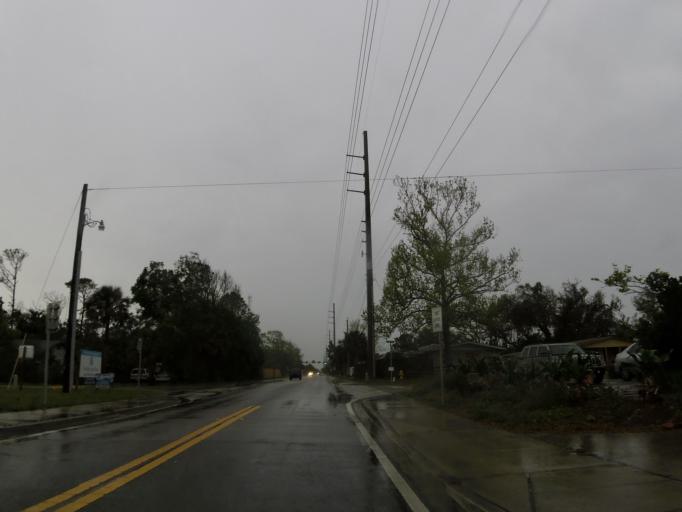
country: US
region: Florida
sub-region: Duval County
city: Jacksonville Beach
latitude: 30.2729
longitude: -81.3955
